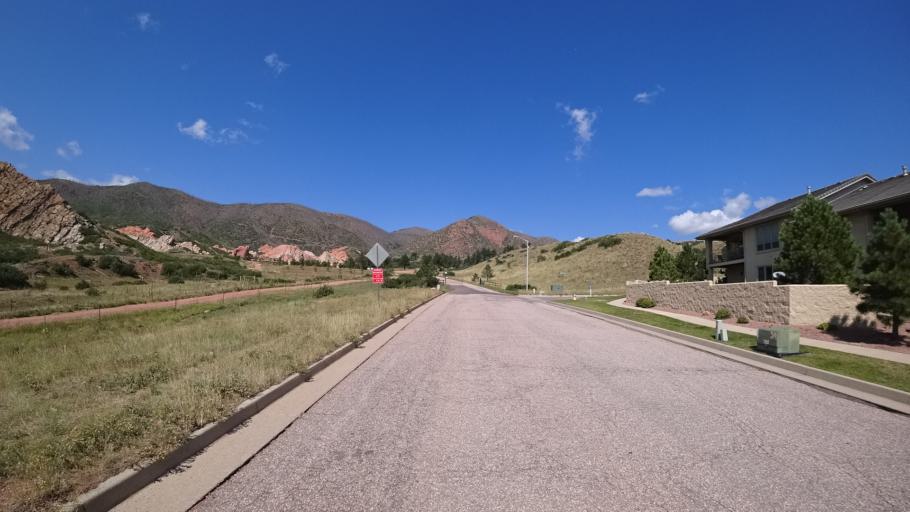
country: US
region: Colorado
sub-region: El Paso County
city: Manitou Springs
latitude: 38.9159
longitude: -104.8780
